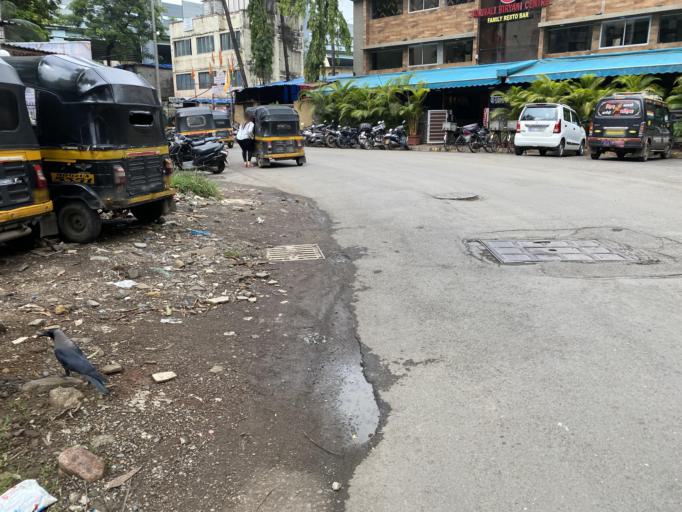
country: IN
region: Maharashtra
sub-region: Mumbai Suburban
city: Borivli
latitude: 19.2589
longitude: 72.8596
